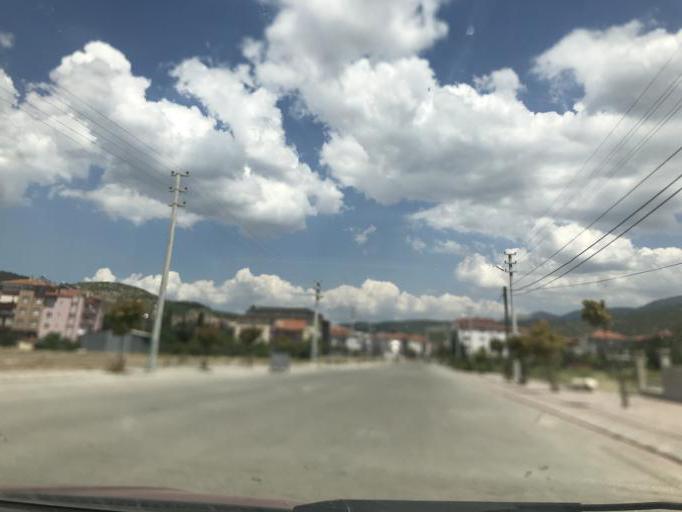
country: TR
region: Denizli
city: Tavas
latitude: 37.5708
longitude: 29.0608
